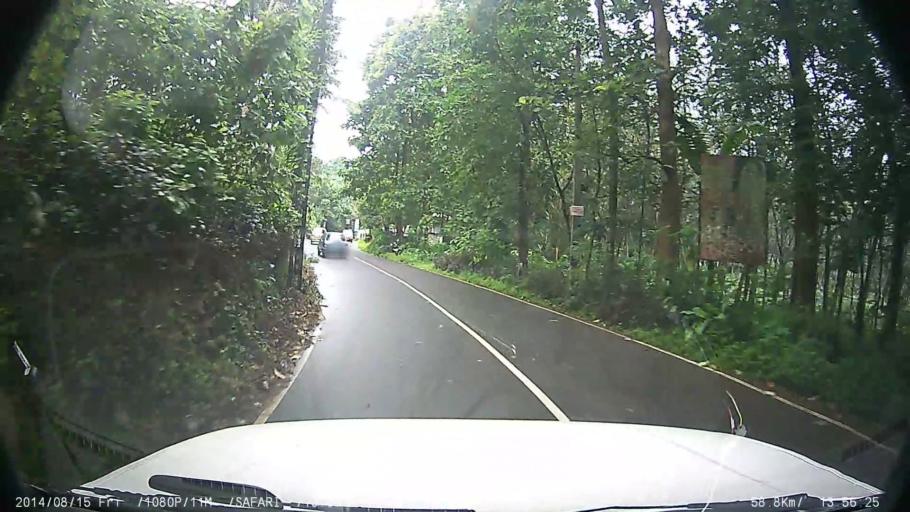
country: IN
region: Kerala
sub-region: Kottayam
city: Lalam
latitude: 9.7177
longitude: 76.6613
